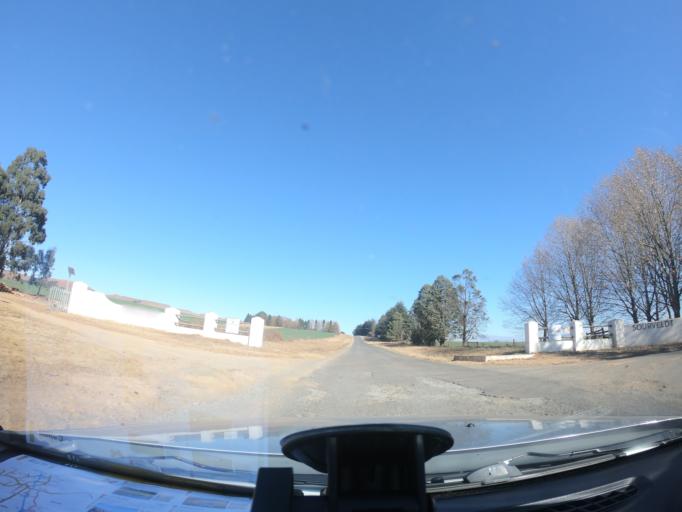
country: ZA
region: KwaZulu-Natal
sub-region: uMgungundlovu District Municipality
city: Mooirivier
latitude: -29.3270
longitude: 29.8277
